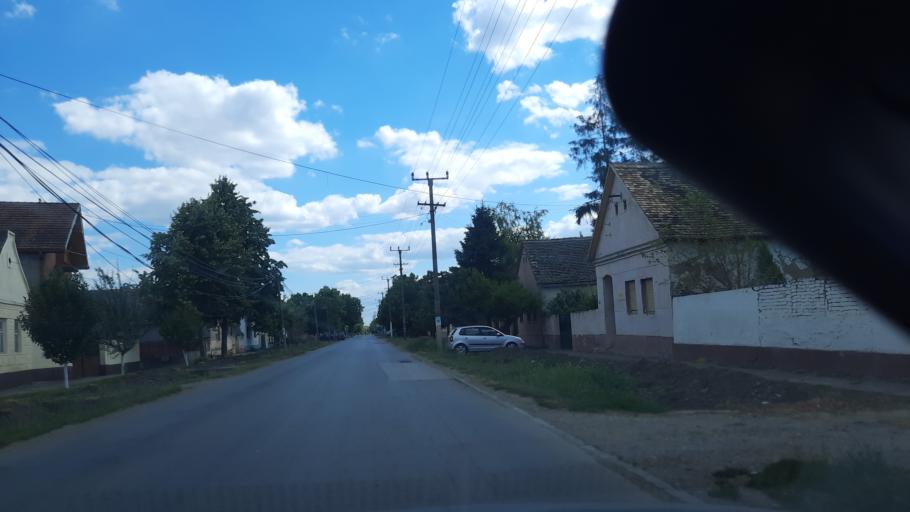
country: RS
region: Autonomna Pokrajina Vojvodina
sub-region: Sremski Okrug
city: Pecinci
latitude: 44.9305
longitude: 20.0072
